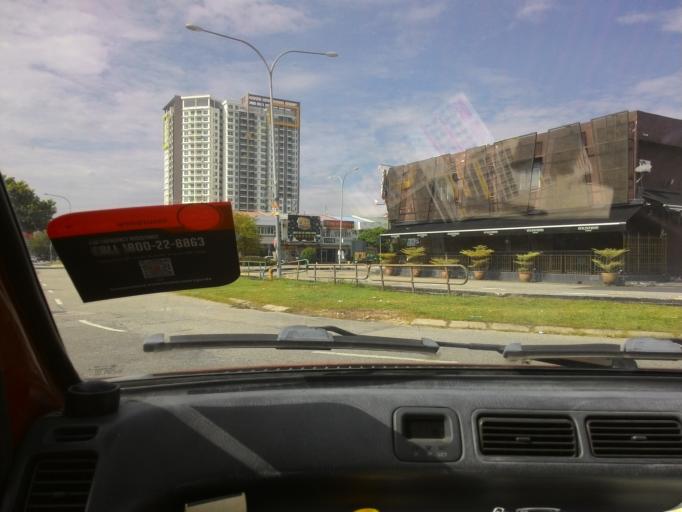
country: MY
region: Perak
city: Ipoh
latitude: 4.6176
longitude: 101.1186
